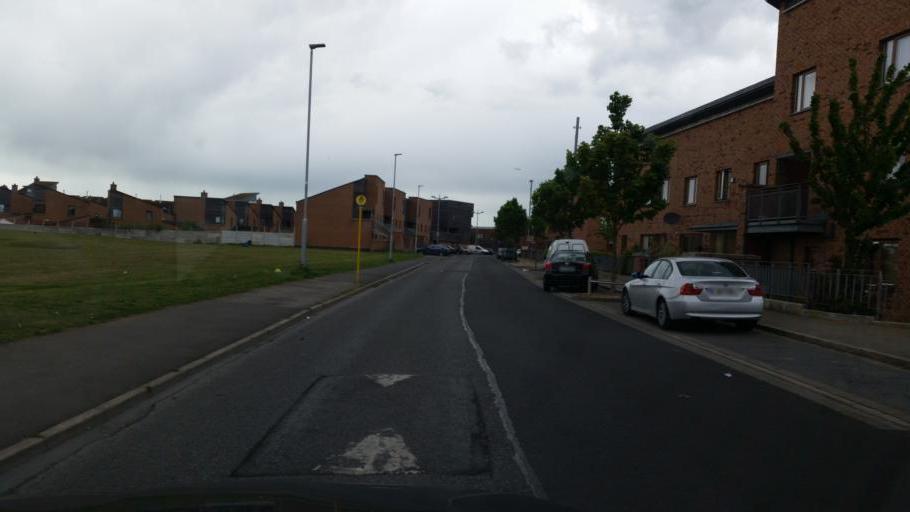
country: IE
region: Leinster
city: Ballymun
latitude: 53.3960
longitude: -6.2736
